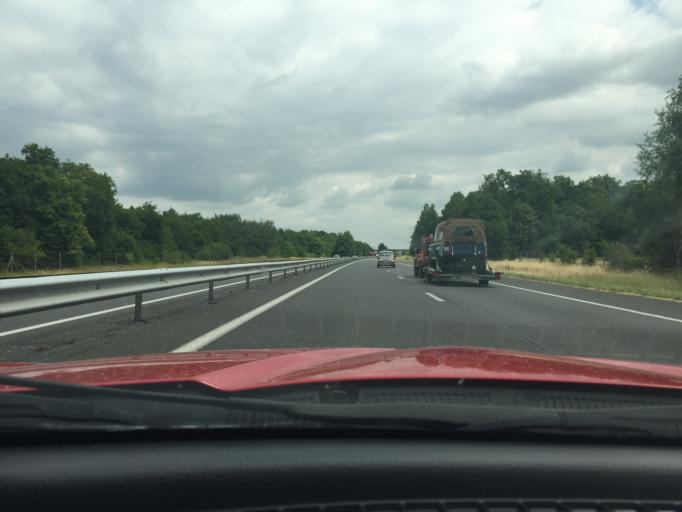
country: FR
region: Picardie
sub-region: Departement de l'Aisne
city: Liesse-Notre-Dame
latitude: 49.5637
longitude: 3.7762
